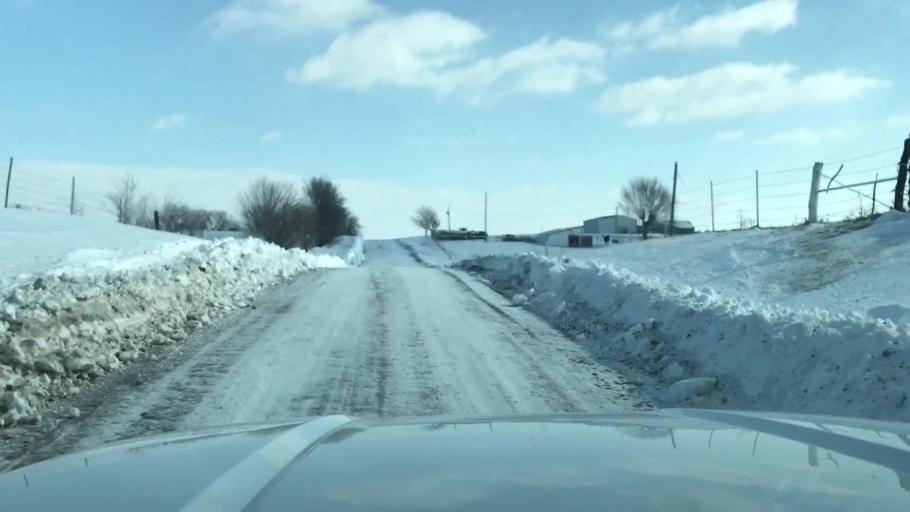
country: US
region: Missouri
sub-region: Nodaway County
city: Maryville
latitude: 40.3868
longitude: -94.7125
